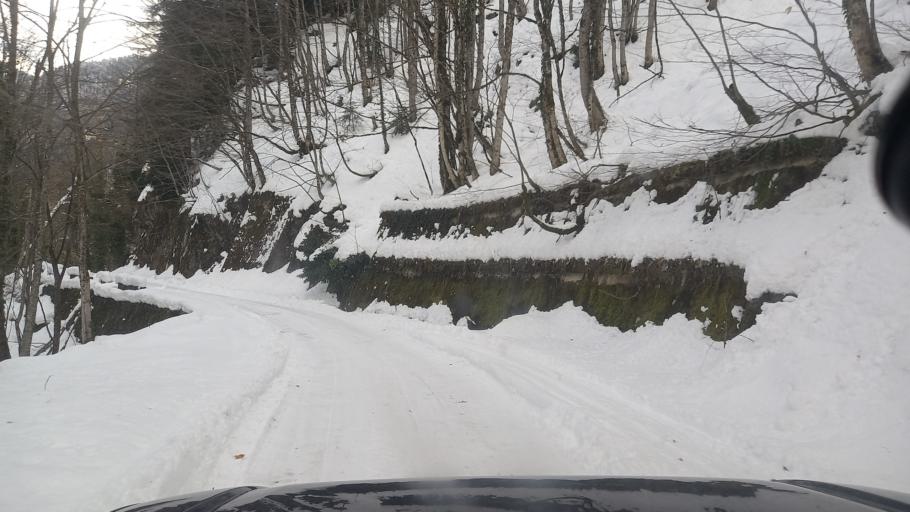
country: GE
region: Abkhazia
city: Gagra
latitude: 43.4789
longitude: 40.5567
